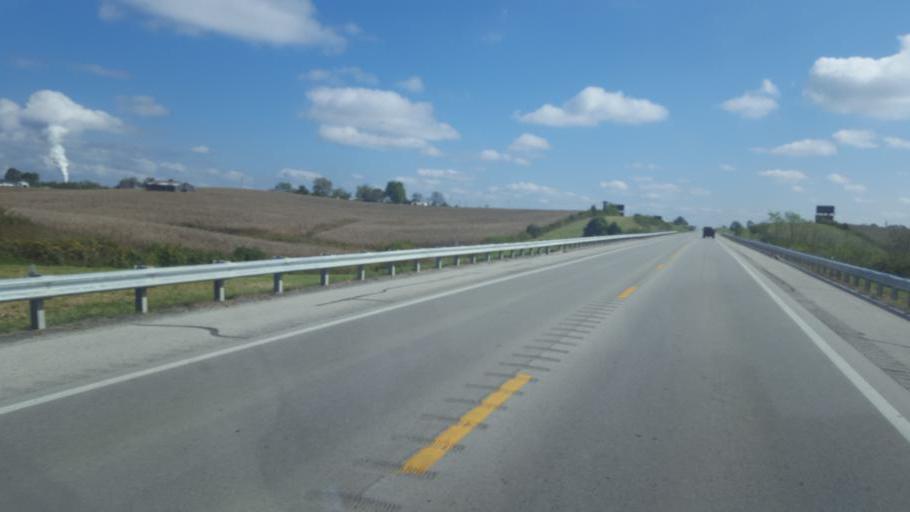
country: US
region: Kentucky
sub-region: Mason County
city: Maysville
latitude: 38.6004
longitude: -83.7469
